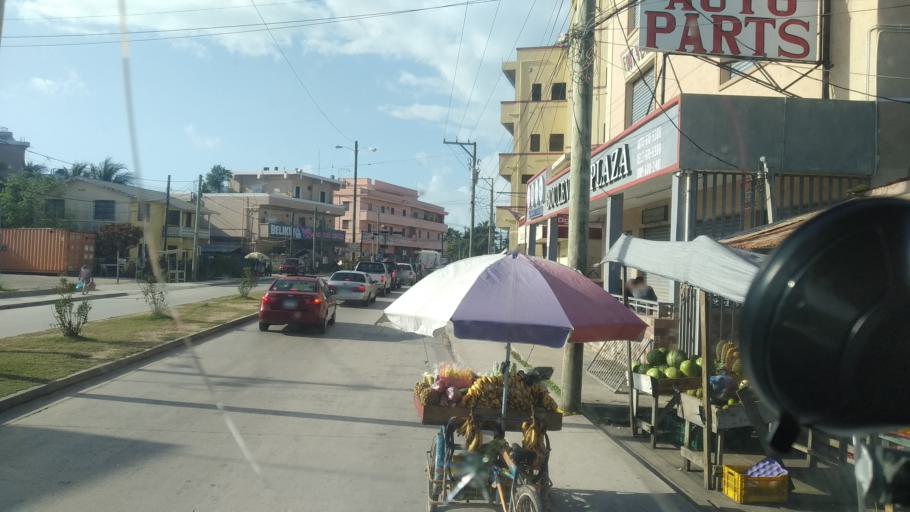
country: BZ
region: Belize
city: Belize City
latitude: 17.4915
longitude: -88.1991
